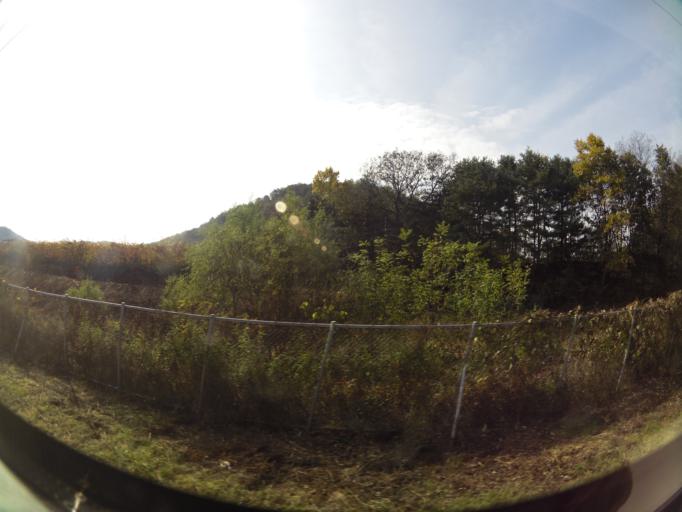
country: KR
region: Chungcheongbuk-do
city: Cheongju-si
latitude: 36.6342
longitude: 127.2885
